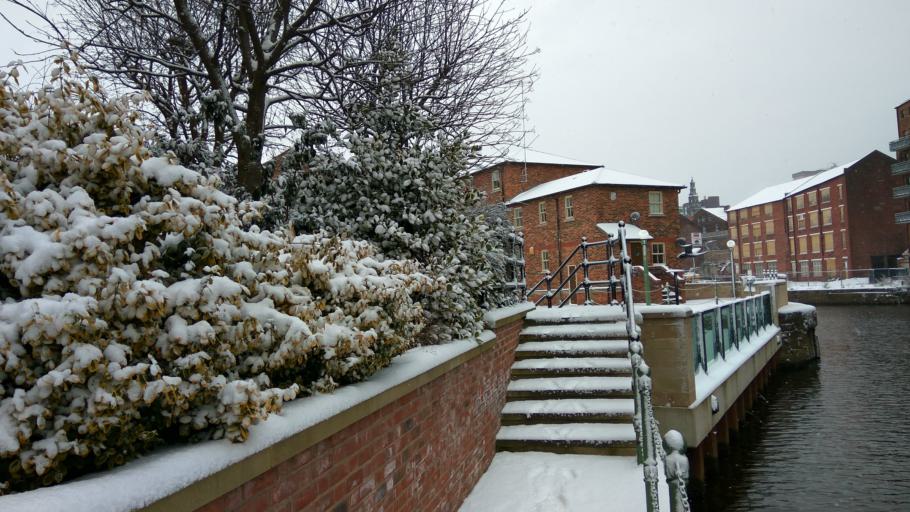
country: GB
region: England
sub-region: City and Borough of Leeds
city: Leeds
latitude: 53.7943
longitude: -1.5382
